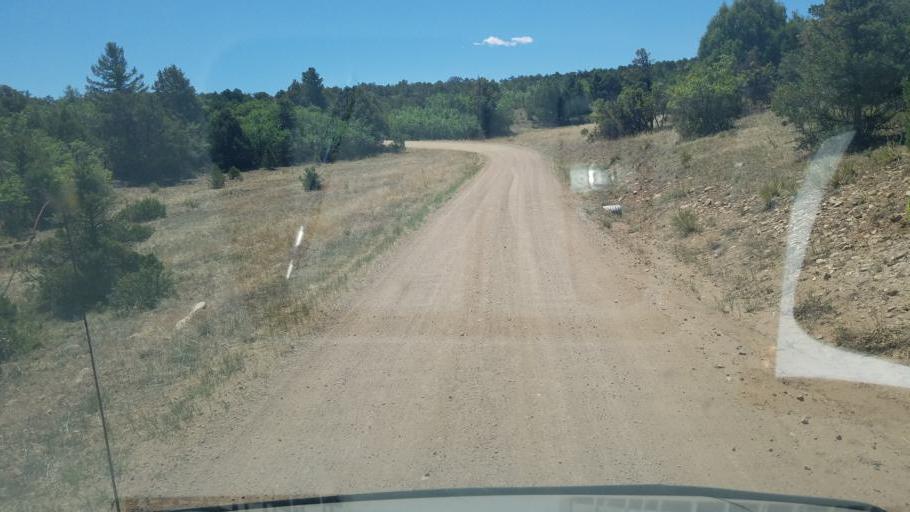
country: US
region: Colorado
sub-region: Custer County
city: Westcliffe
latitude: 38.3034
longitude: -105.6714
